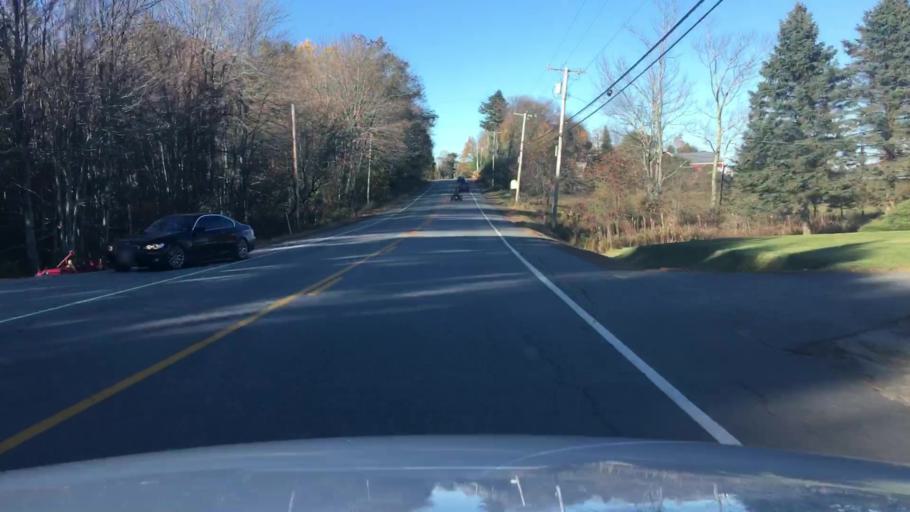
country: US
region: Maine
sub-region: Sagadahoc County
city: Topsham
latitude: 44.0450
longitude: -69.9407
